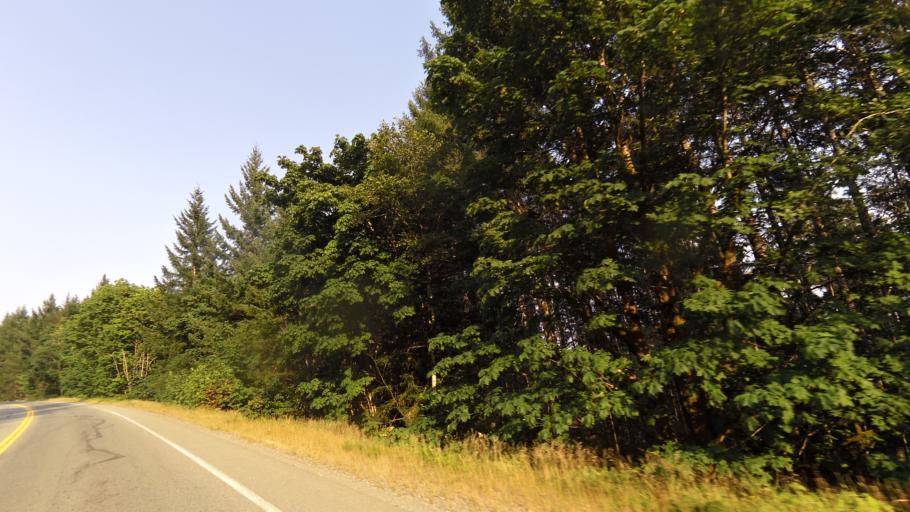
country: CA
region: British Columbia
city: Port Alberni
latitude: 49.2798
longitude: -125.0237
